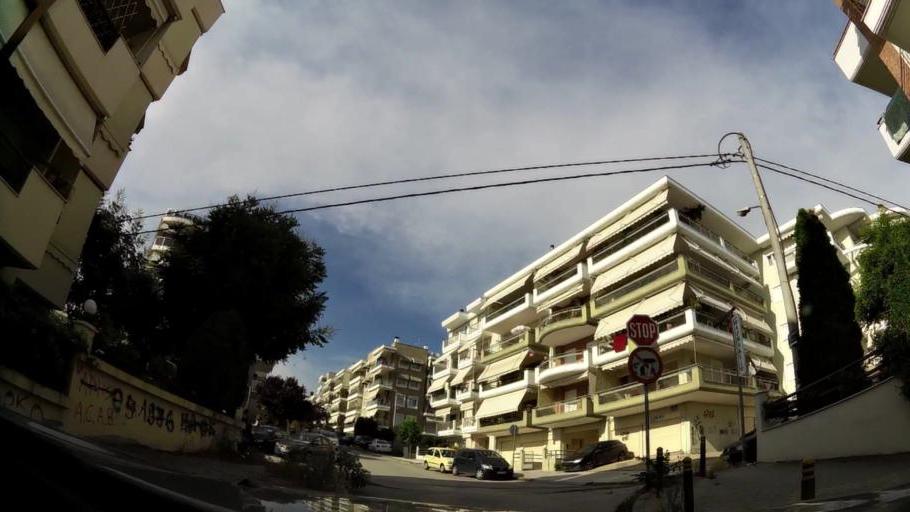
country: GR
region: Central Macedonia
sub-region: Nomos Thessalonikis
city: Kalamaria
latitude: 40.5757
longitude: 22.9577
